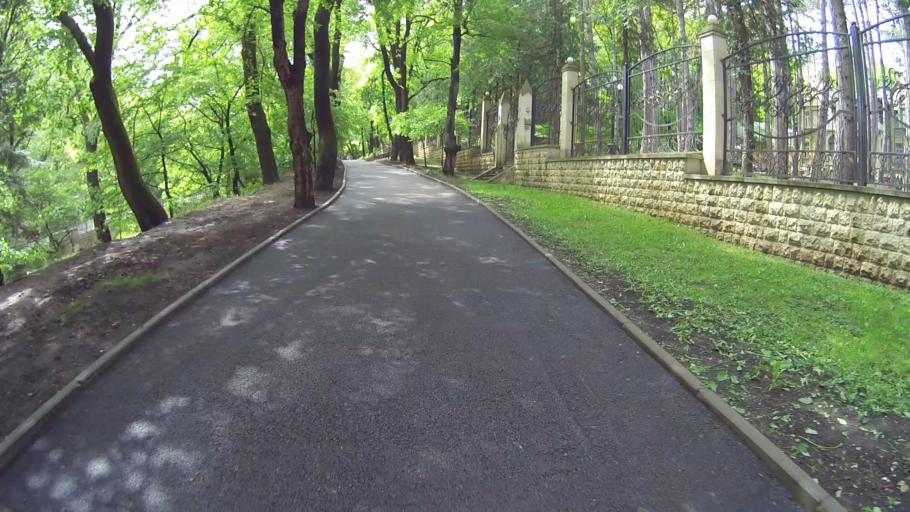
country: RU
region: Stavropol'skiy
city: Kislovodsk
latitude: 43.8965
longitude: 42.7176
